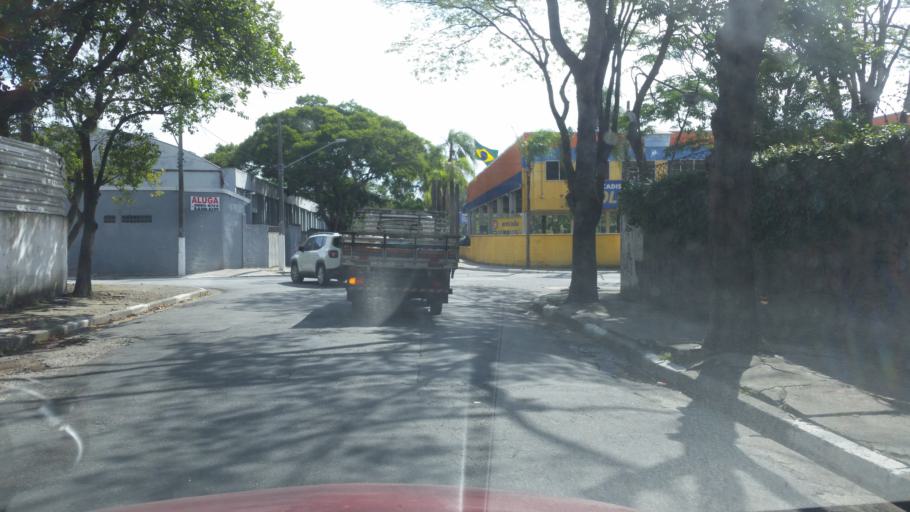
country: BR
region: Sao Paulo
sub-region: Diadema
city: Diadema
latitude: -23.6734
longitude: -46.6992
